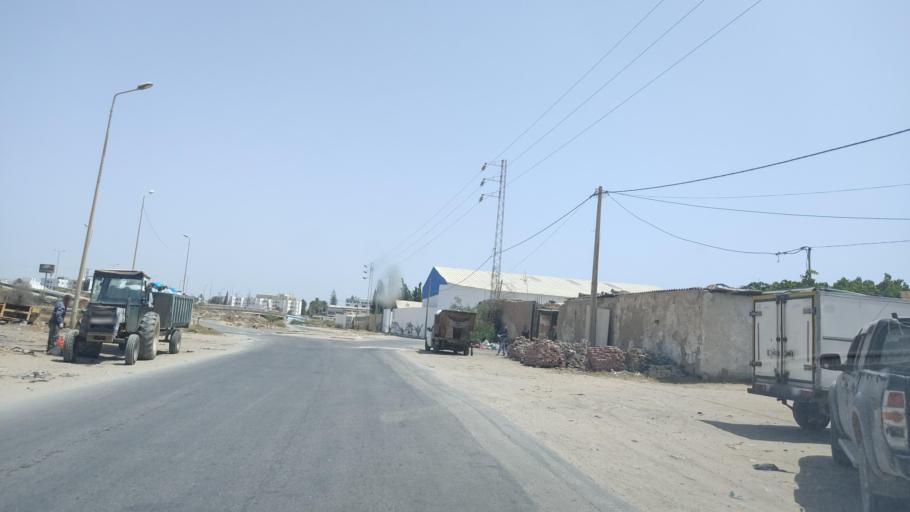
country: TN
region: Safaqis
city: Sfax
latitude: 34.7066
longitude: 10.7224
